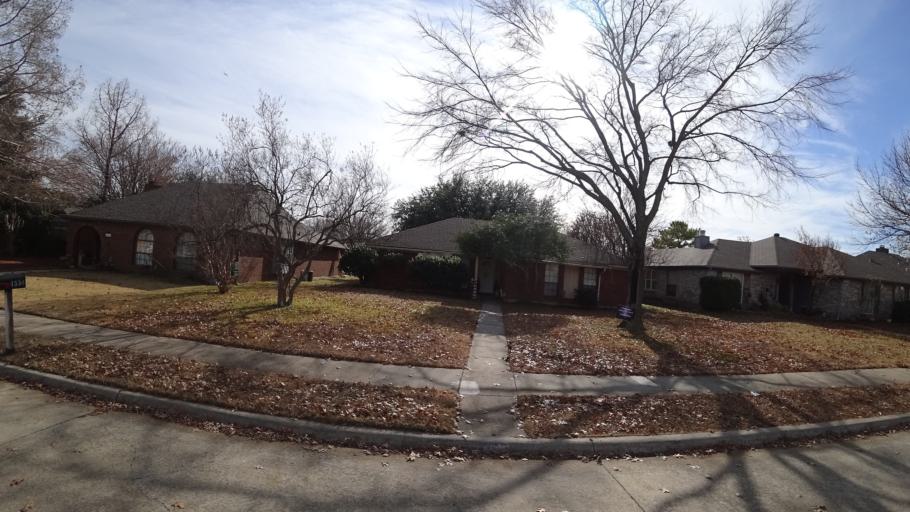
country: US
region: Texas
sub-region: Denton County
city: Highland Village
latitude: 33.0594
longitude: -97.0386
